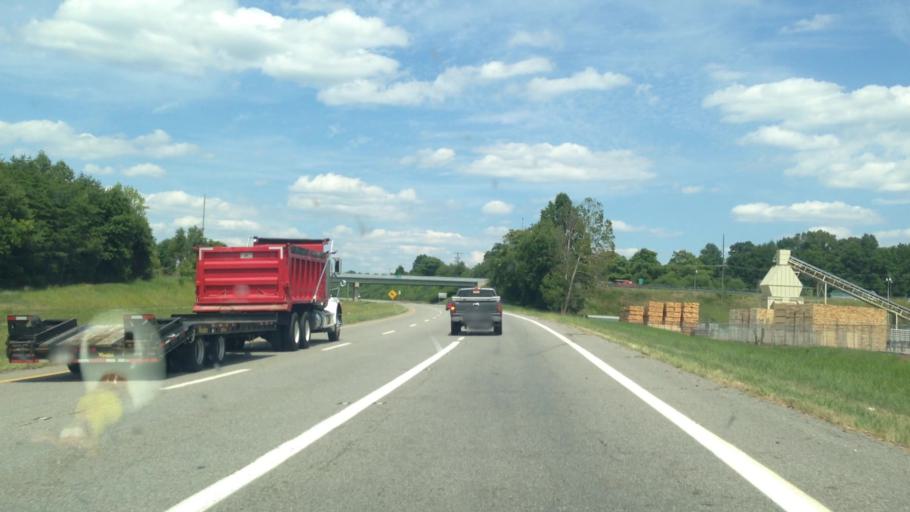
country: US
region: Virginia
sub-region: Henry County
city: Chatmoss
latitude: 36.6228
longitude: -79.8549
